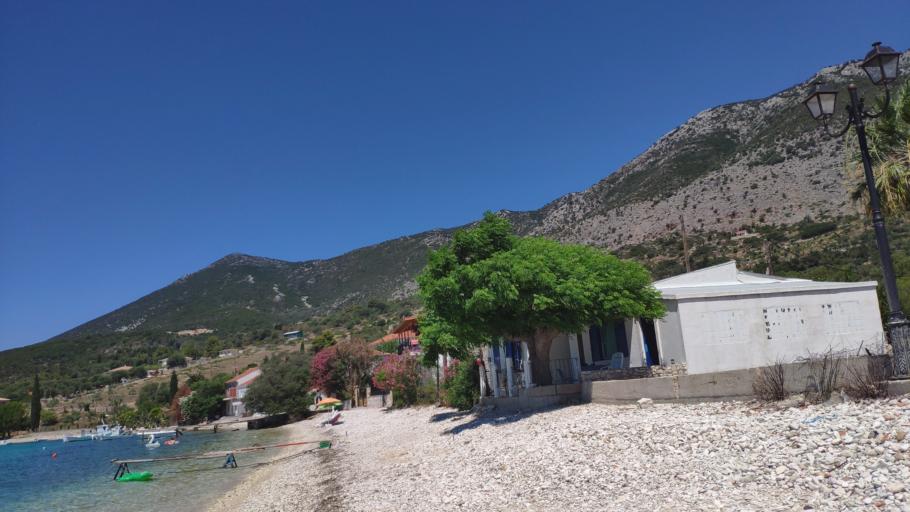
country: GR
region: West Greece
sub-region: Nomos Aitolias kai Akarnanias
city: Kandila
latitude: 38.6161
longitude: 20.9254
